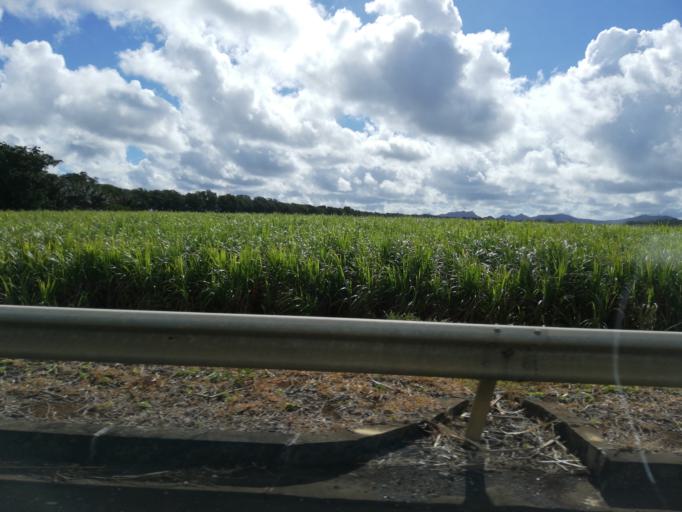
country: MU
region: Grand Port
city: Beau Vallon
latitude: -20.4063
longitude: 57.6750
